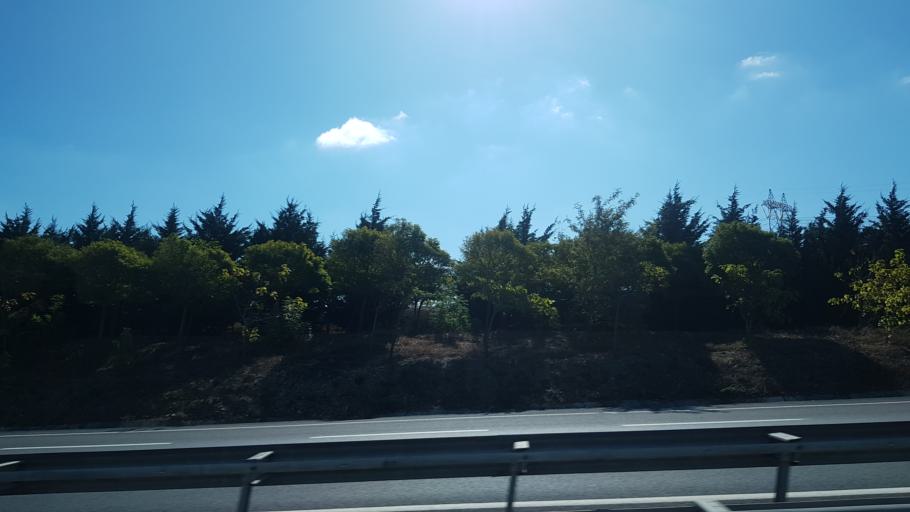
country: TR
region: Istanbul
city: Canta
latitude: 41.0942
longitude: 28.1469
